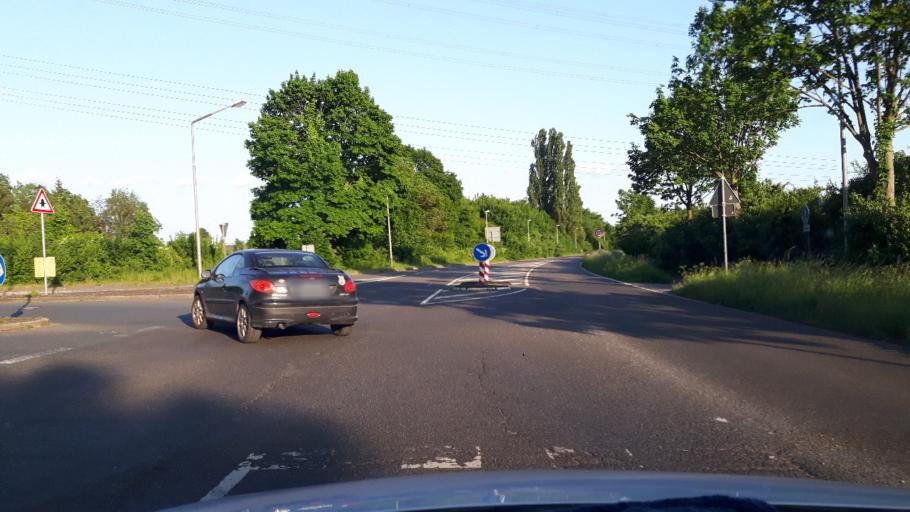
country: DE
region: North Rhine-Westphalia
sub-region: Regierungsbezirk Dusseldorf
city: Ratingen
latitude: 51.3397
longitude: 6.8180
